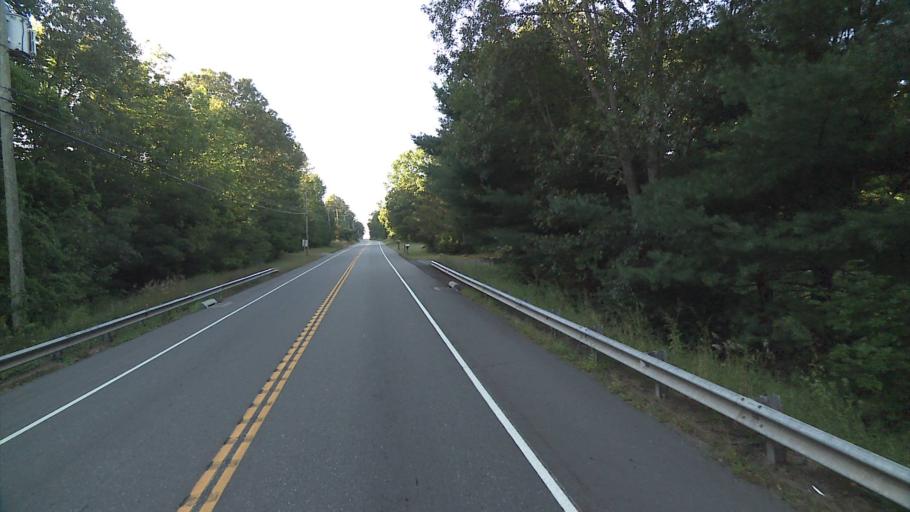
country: US
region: Connecticut
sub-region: Tolland County
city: South Coventry
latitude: 41.8194
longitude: -72.3102
